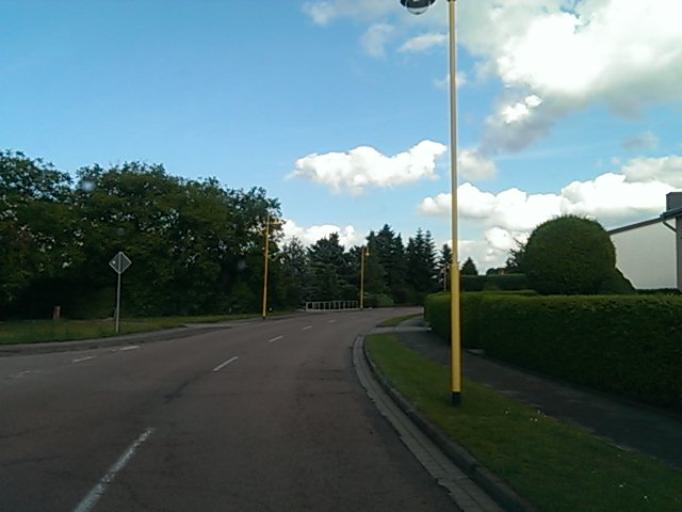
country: DE
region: Saxony-Anhalt
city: Nudersdorf
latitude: 51.9643
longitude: 12.5263
